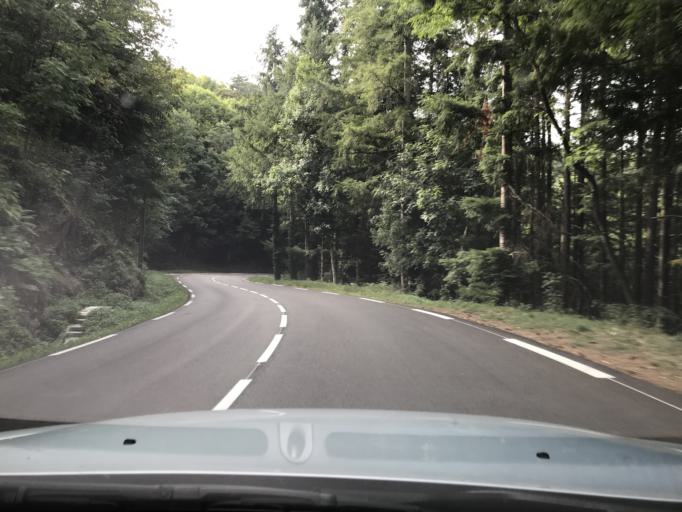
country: FR
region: Rhone-Alpes
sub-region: Departement de l'Ardeche
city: Lamastre
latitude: 44.9820
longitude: 4.6113
